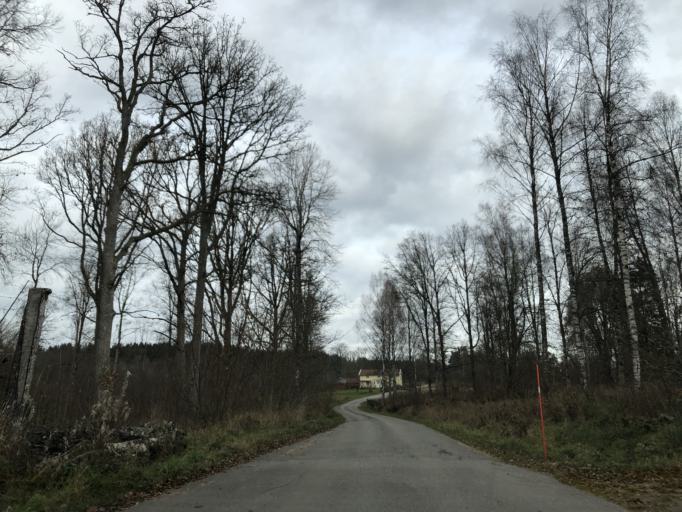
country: SE
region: Vaestra Goetaland
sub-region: Ulricehamns Kommun
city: Ulricehamn
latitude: 57.7334
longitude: 13.3701
